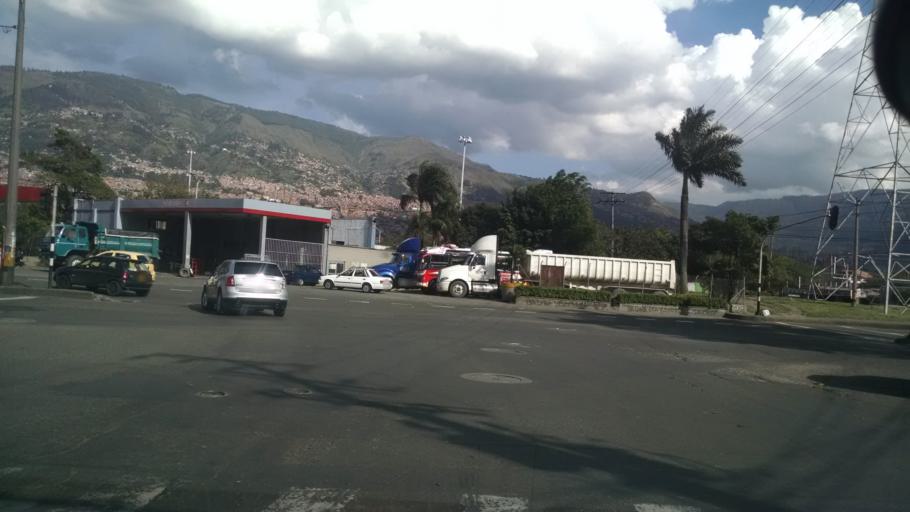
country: CO
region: Antioquia
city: Medellin
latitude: 6.2765
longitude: -75.5737
